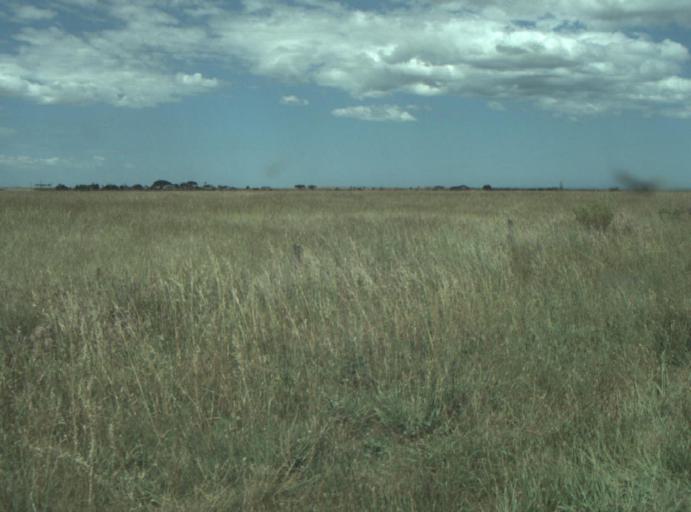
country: AU
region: Victoria
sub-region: Wyndham
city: Little River
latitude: -37.8969
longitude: 144.4646
